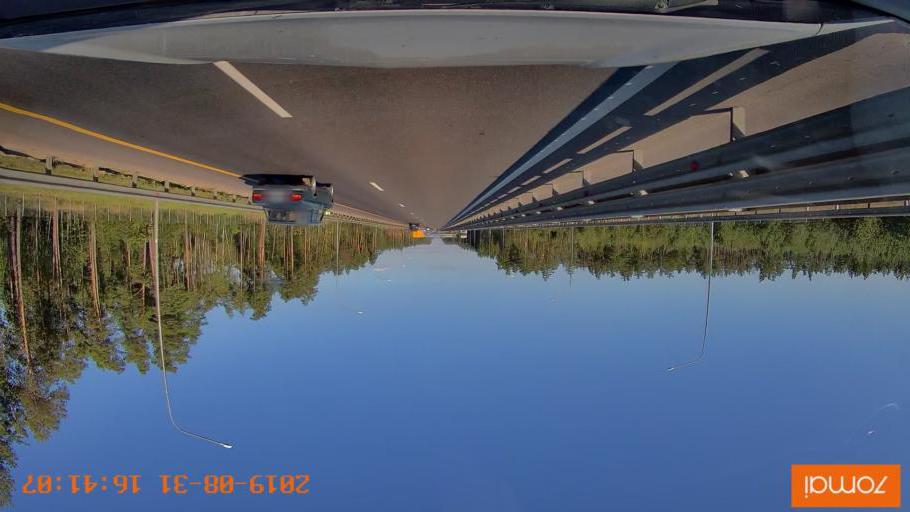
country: RU
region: Kaluga
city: Kurovskoye
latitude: 54.5754
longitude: 36.0615
